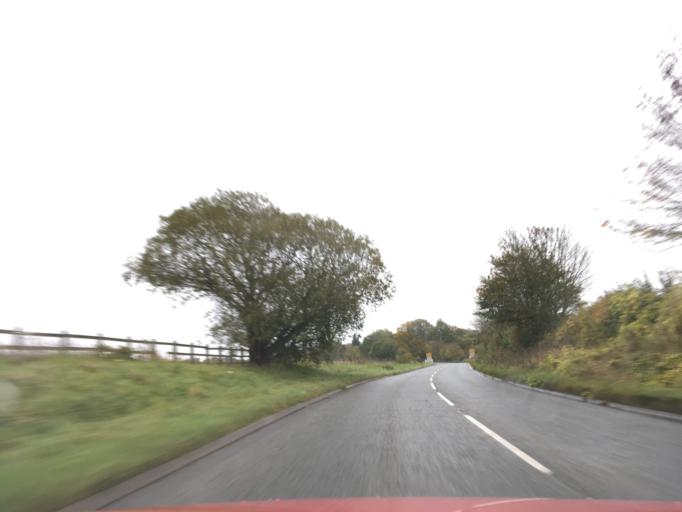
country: GB
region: England
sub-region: West Berkshire
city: Wickham
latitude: 51.4449
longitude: -1.4413
